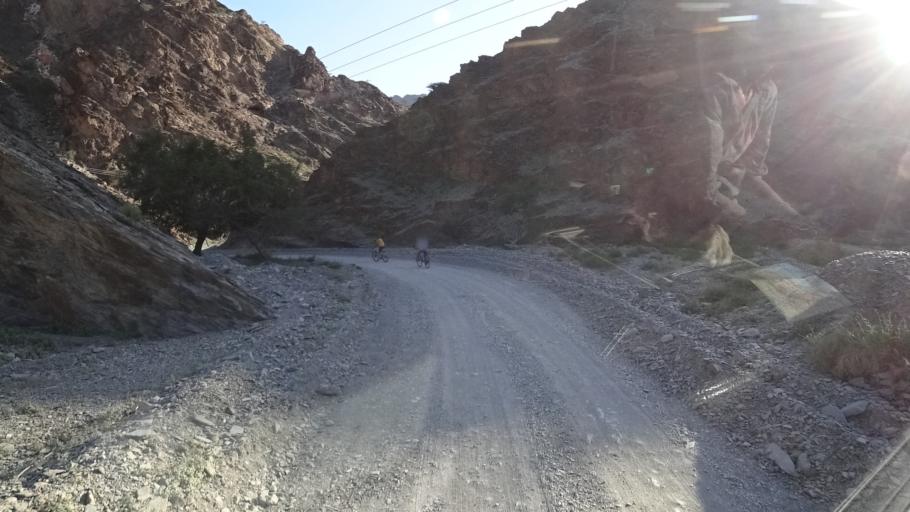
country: OM
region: Al Batinah
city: Rustaq
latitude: 23.2620
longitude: 57.3965
